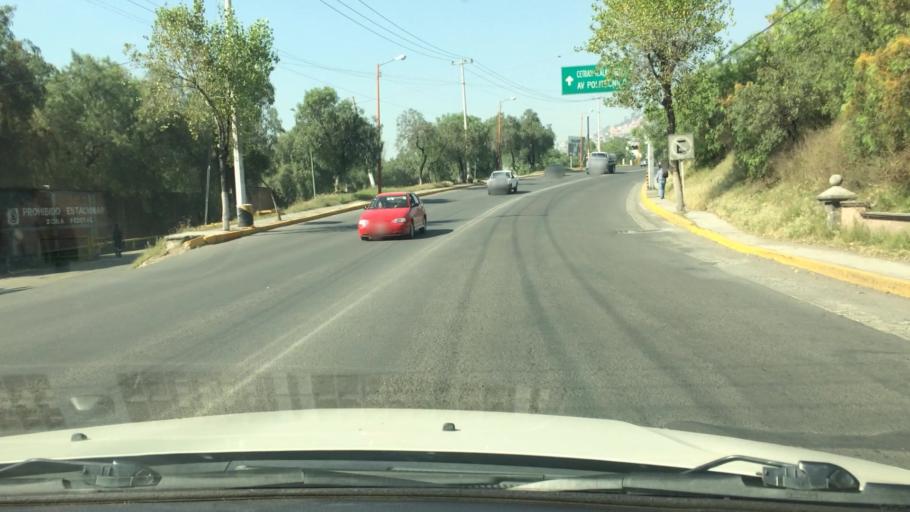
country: MX
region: Mexico
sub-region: Tlalnepantla de Baz
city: Puerto Escondido (Tepeolulco Puerto Escondido)
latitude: 19.5256
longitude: -99.1070
